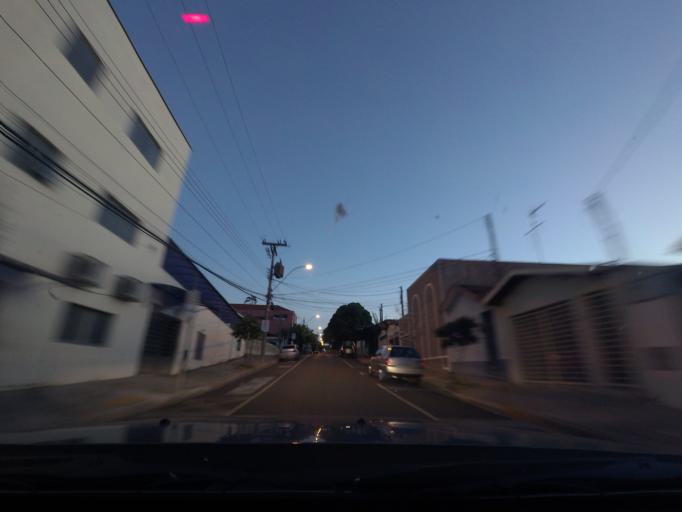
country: BR
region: Sao Paulo
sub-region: Piracicaba
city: Piracicaba
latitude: -22.7175
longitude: -47.6318
